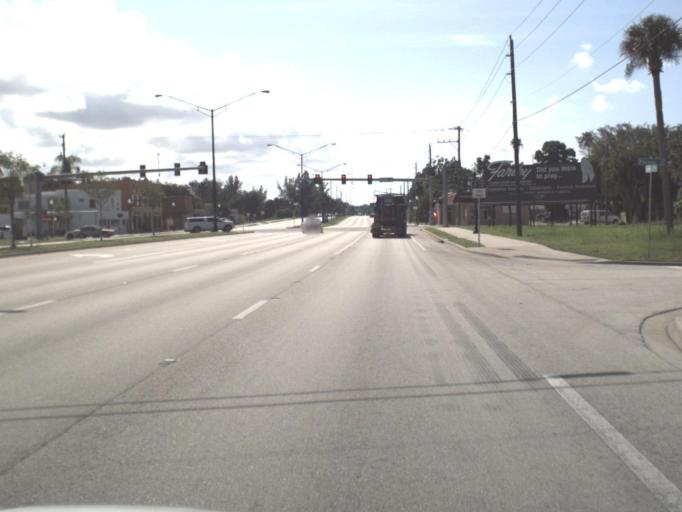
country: US
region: Florida
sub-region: Sarasota County
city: Nokomis
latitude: 27.1168
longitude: -82.4501
